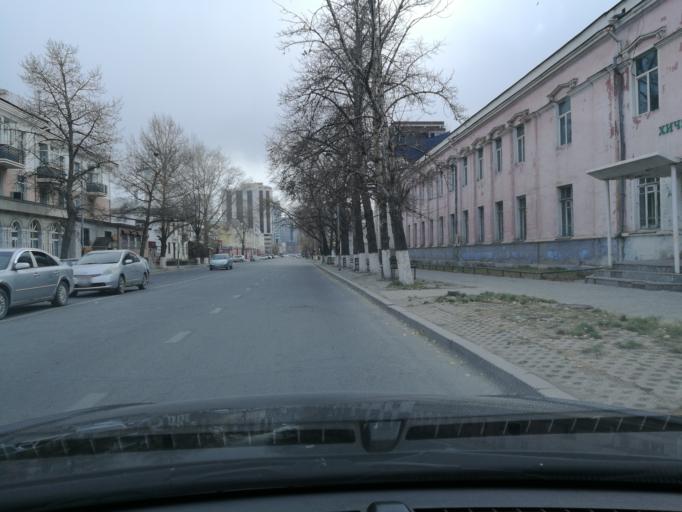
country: MN
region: Ulaanbaatar
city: Ulaanbaatar
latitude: 47.9259
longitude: 106.9178
